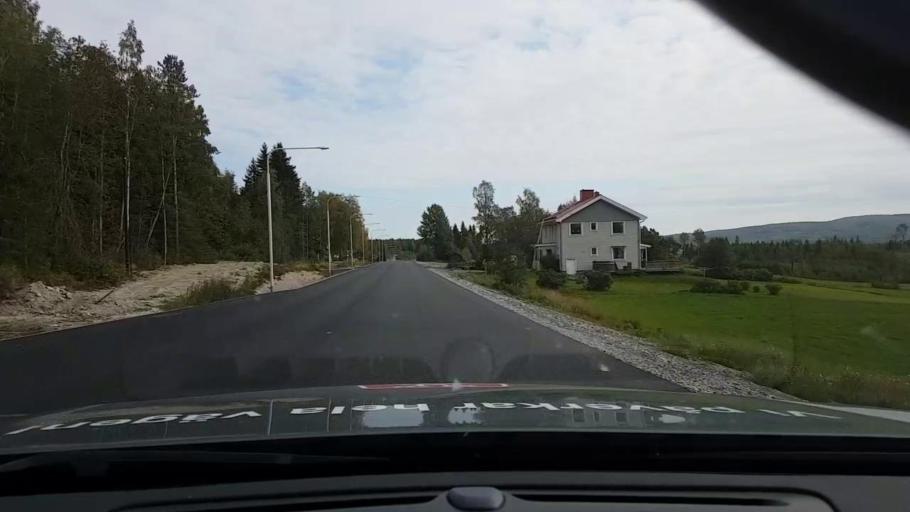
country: SE
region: Vaesternorrland
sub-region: OErnskoeldsviks Kommun
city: Bjasta
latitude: 63.2930
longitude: 18.4821
